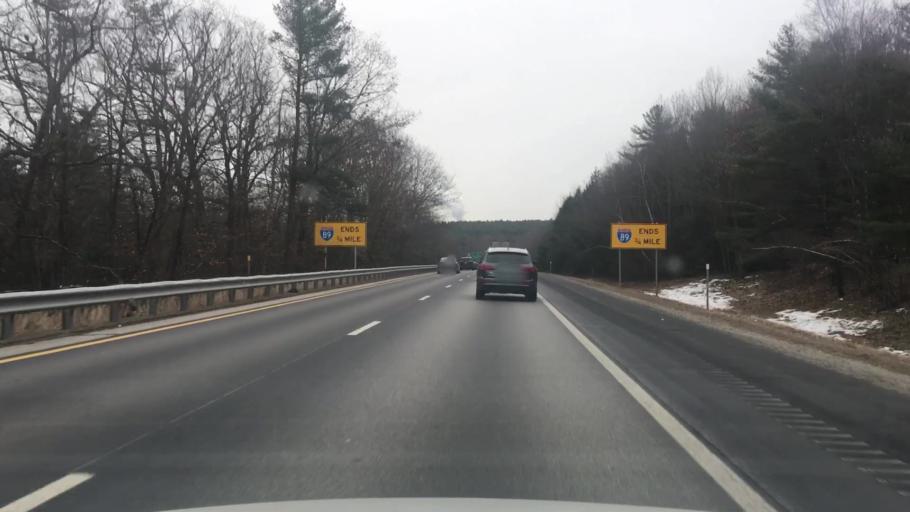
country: US
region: New Hampshire
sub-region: Merrimack County
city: Concord
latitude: 43.1699
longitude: -71.5448
